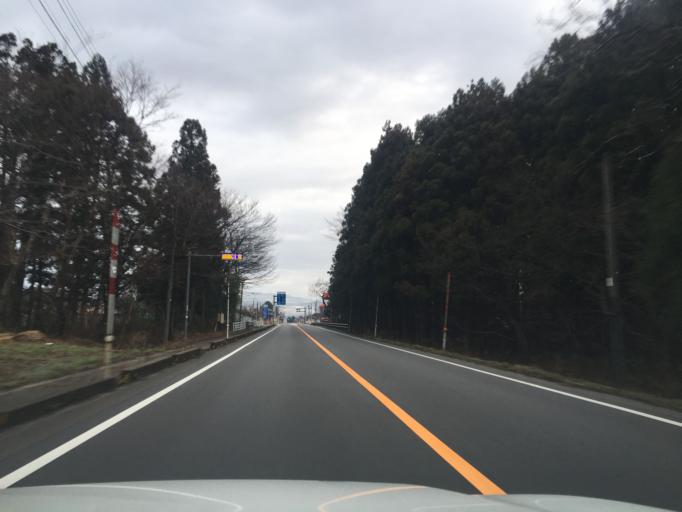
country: JP
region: Niigata
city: Murakami
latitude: 38.3085
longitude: 139.5446
